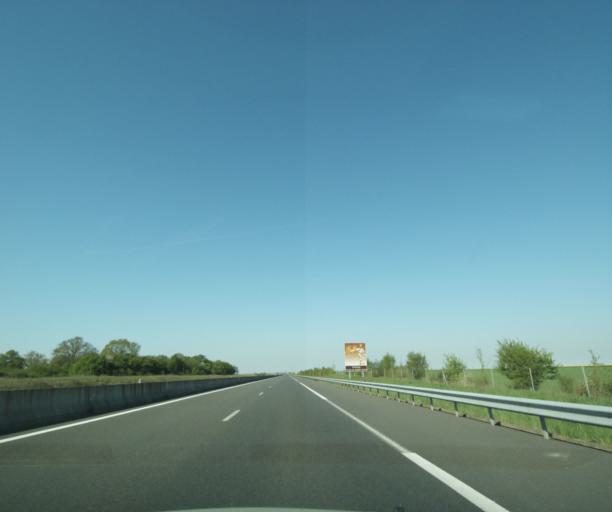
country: FR
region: Centre
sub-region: Departement du Loiret
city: Chevilly
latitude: 48.0483
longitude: 1.9092
